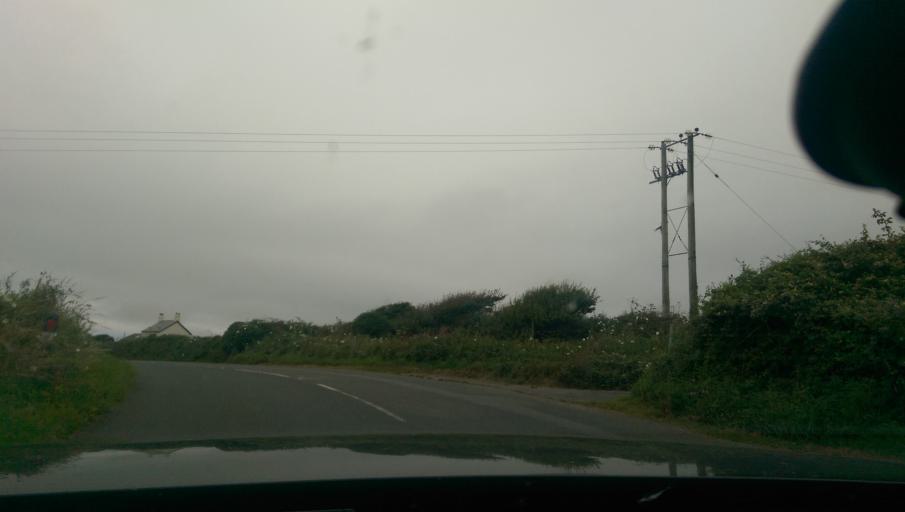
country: GB
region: England
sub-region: Cornwall
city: Saint Just
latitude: 50.1143
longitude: -5.6781
